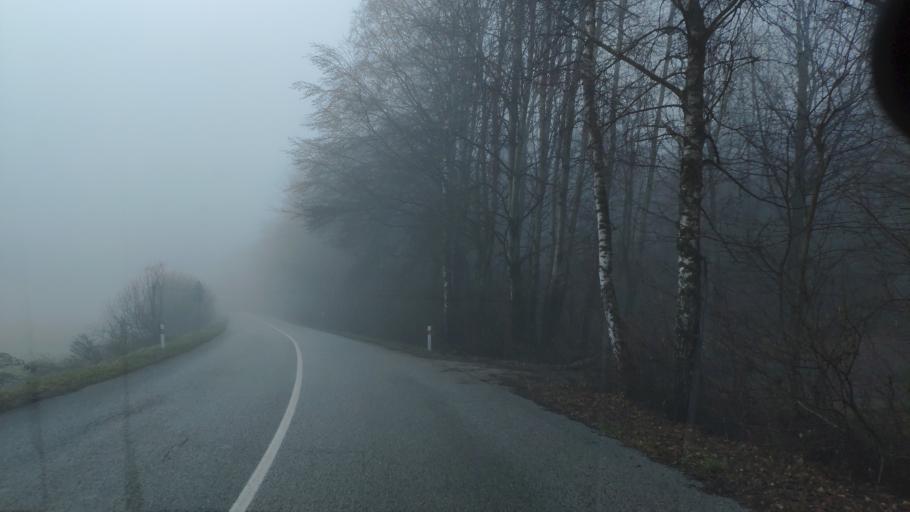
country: SK
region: Banskobystricky
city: Revuca
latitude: 48.6475
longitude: 20.2991
